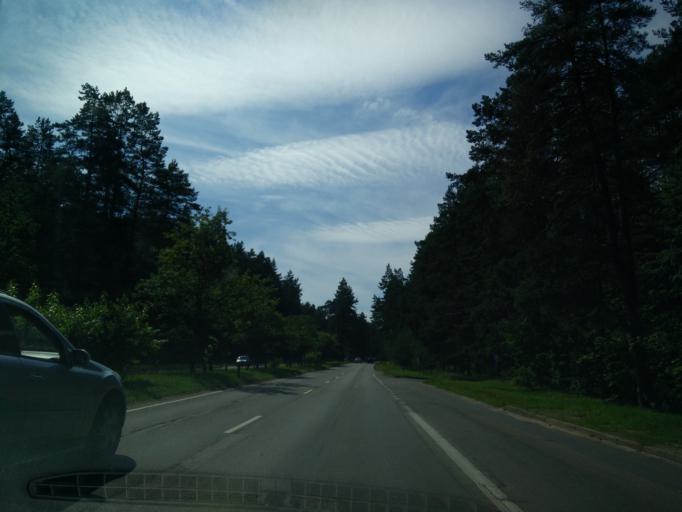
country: LT
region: Vilnius County
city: Rasos
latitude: 54.7483
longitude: 25.3579
